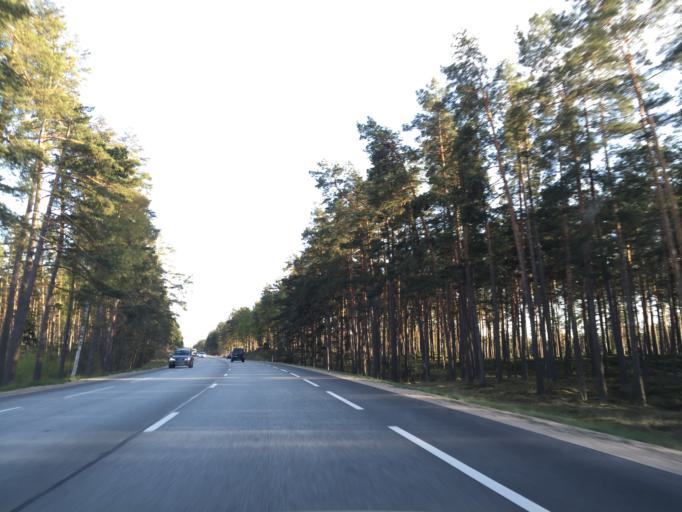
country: LV
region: Carnikava
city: Carnikava
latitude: 57.1789
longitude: 24.3417
